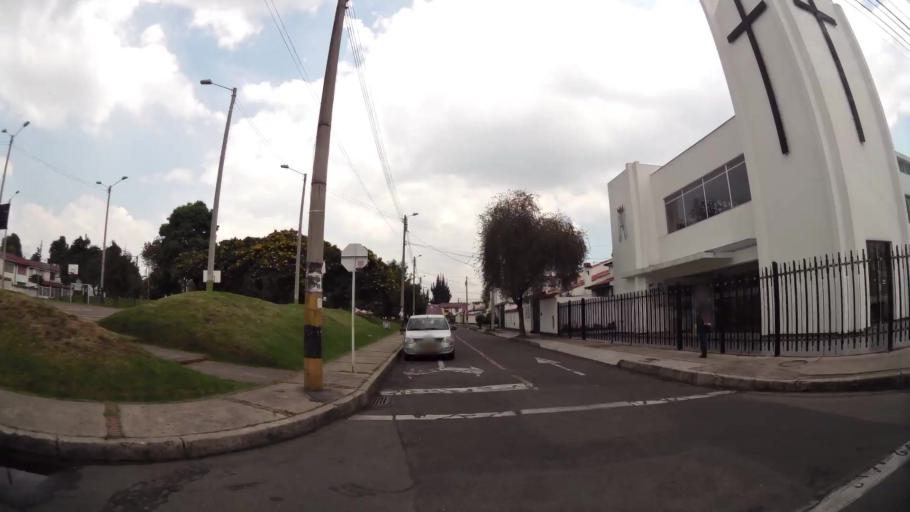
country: CO
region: Cundinamarca
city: Cota
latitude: 4.7547
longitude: -74.0557
